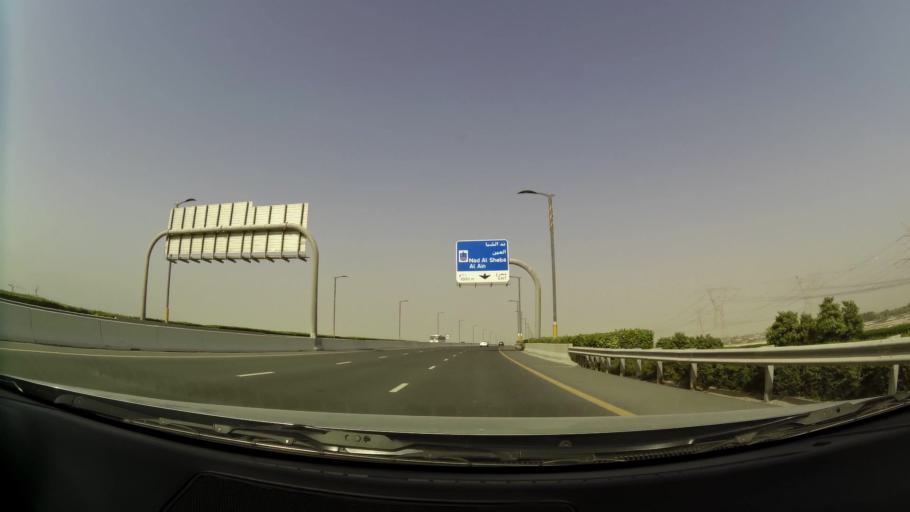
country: AE
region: Dubai
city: Dubai
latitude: 25.1708
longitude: 55.3100
